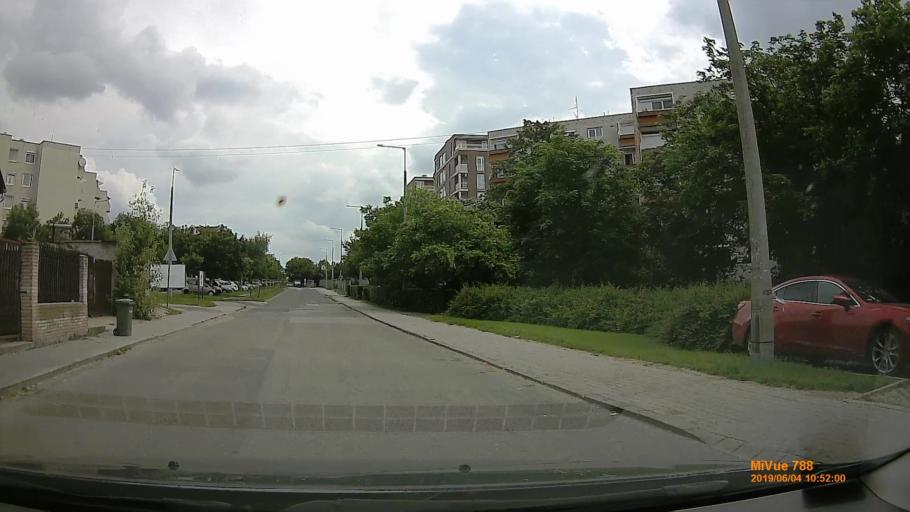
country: HU
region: Budapest
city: Budapest XXII. keruelet
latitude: 47.4084
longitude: 19.0022
